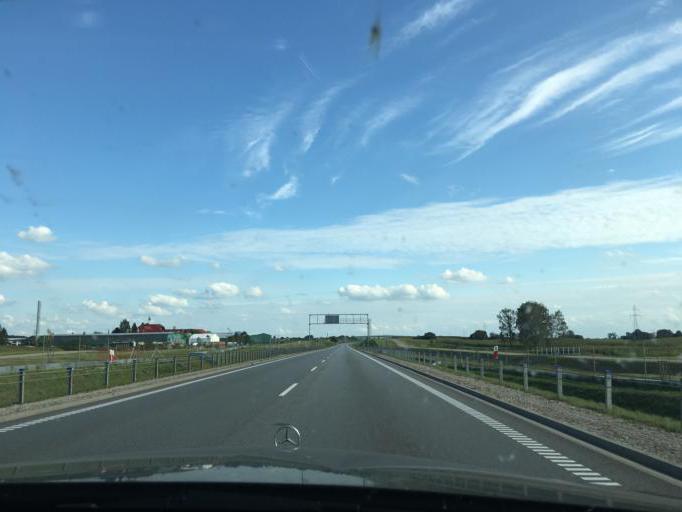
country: PL
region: Podlasie
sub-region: Powiat augustowski
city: Augustow
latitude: 53.8567
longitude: 22.9190
